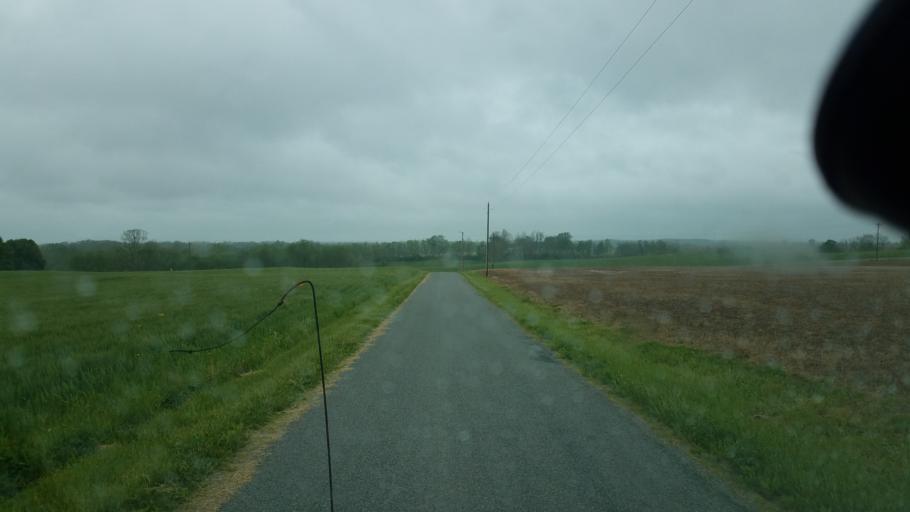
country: US
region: Ohio
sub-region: Highland County
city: Greenfield
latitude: 39.3334
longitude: -83.4569
